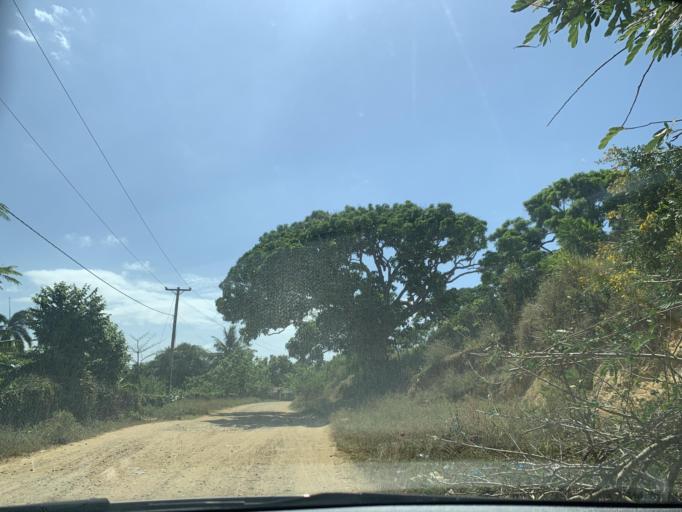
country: DO
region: Puerto Plata
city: Luperon
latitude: 19.8831
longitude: -70.8705
